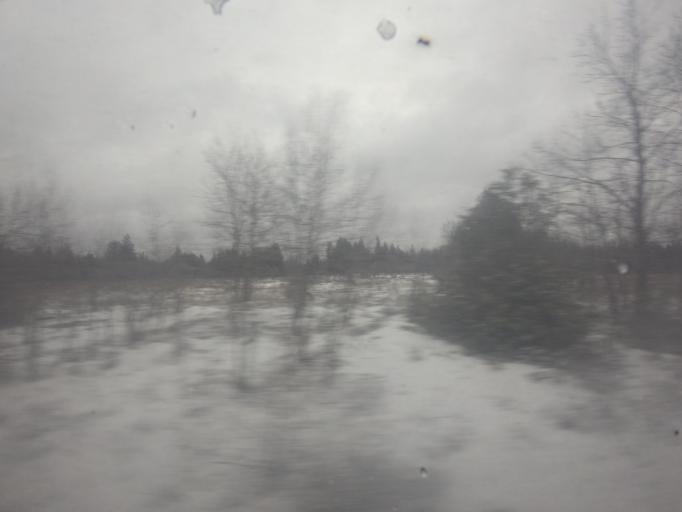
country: CA
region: Ontario
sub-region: Lanark County
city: Smiths Falls
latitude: 44.9987
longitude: -75.9649
